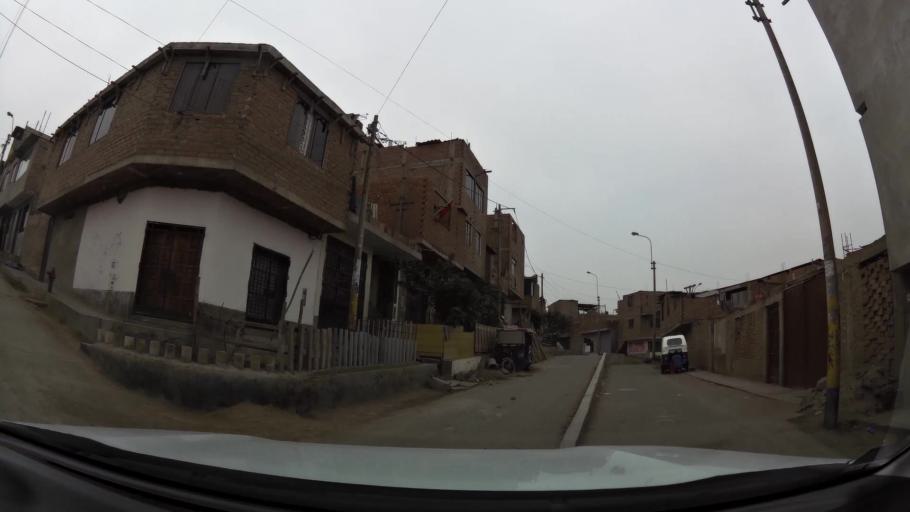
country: PE
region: Lima
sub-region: Lima
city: Surco
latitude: -12.1769
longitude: -76.9687
